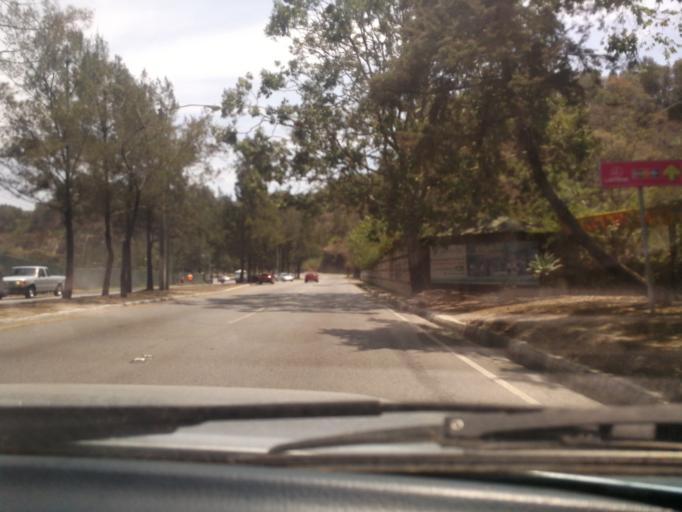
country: GT
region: Guatemala
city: Guatemala City
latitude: 14.6221
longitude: -90.4894
